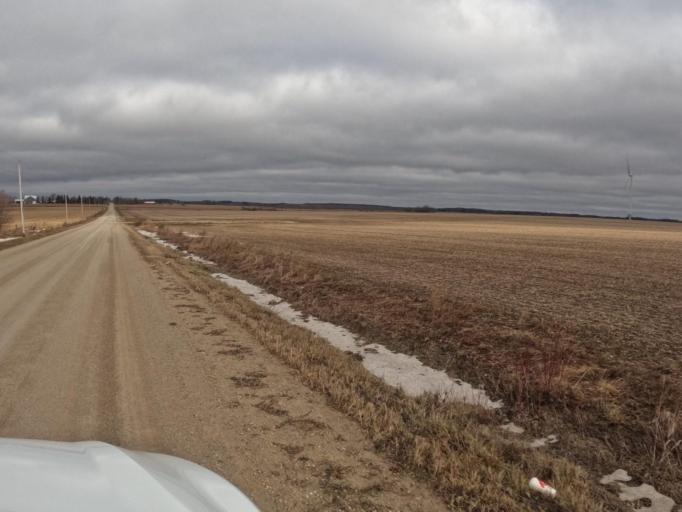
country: CA
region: Ontario
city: Shelburne
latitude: 43.9992
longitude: -80.4092
